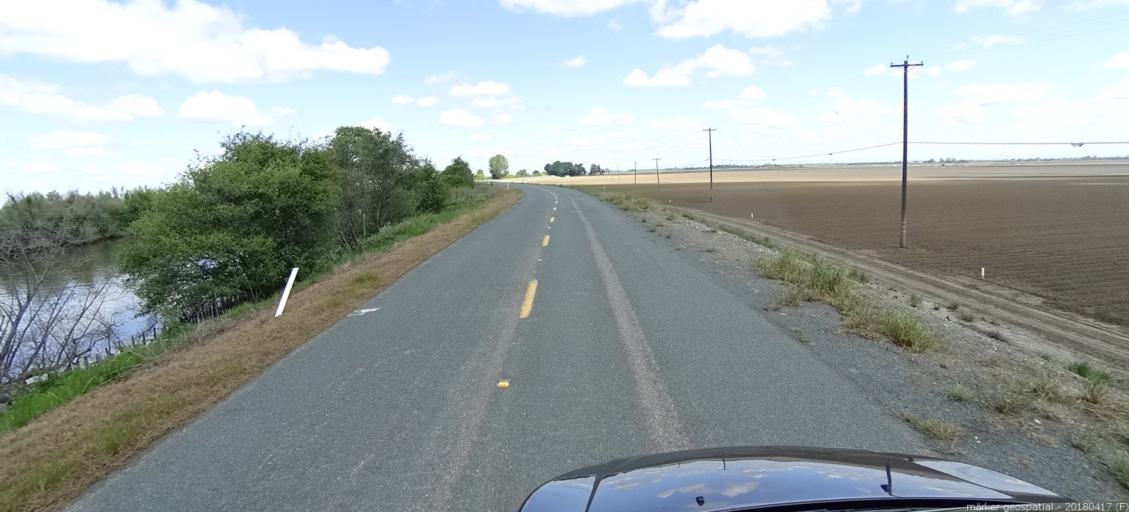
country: US
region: California
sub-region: Sacramento County
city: Walnut Grove
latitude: 38.1864
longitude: -121.5602
